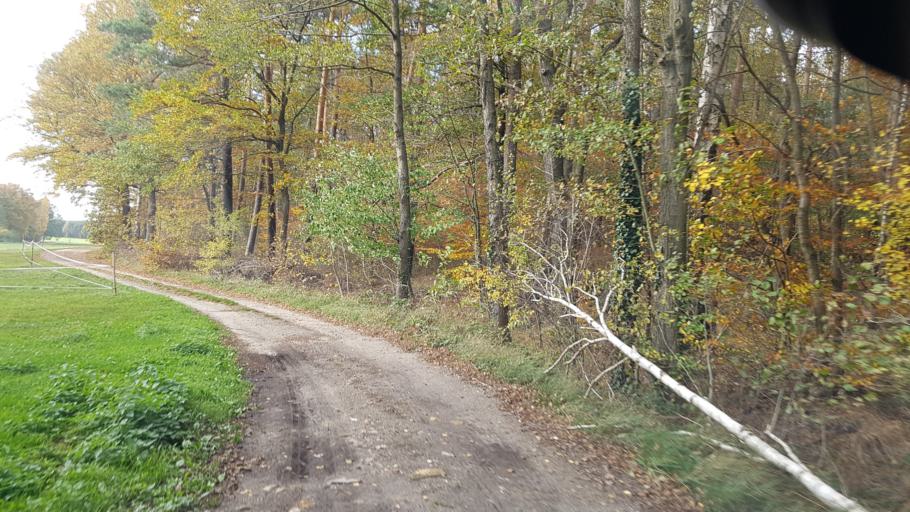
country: DE
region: Saxony
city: Dahlen
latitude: 51.4033
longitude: 12.9785
